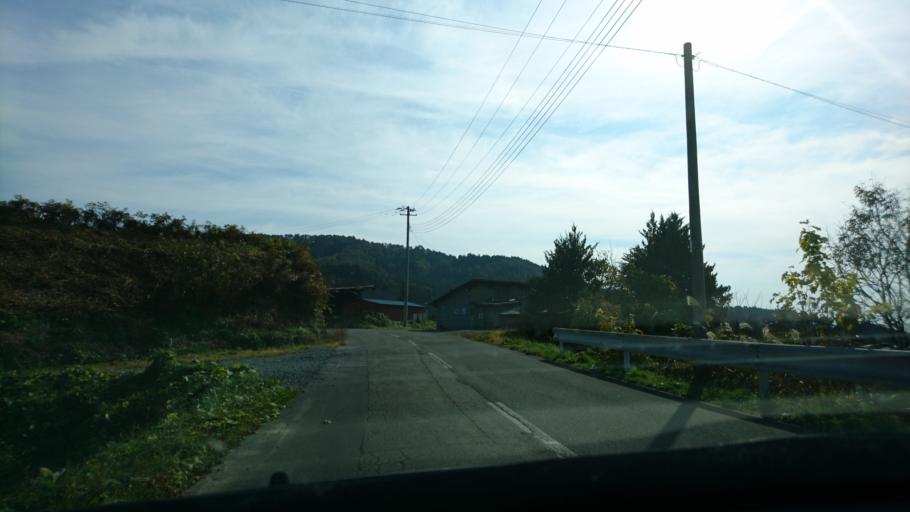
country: JP
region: Iwate
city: Ichinoseki
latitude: 38.9766
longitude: 141.1781
